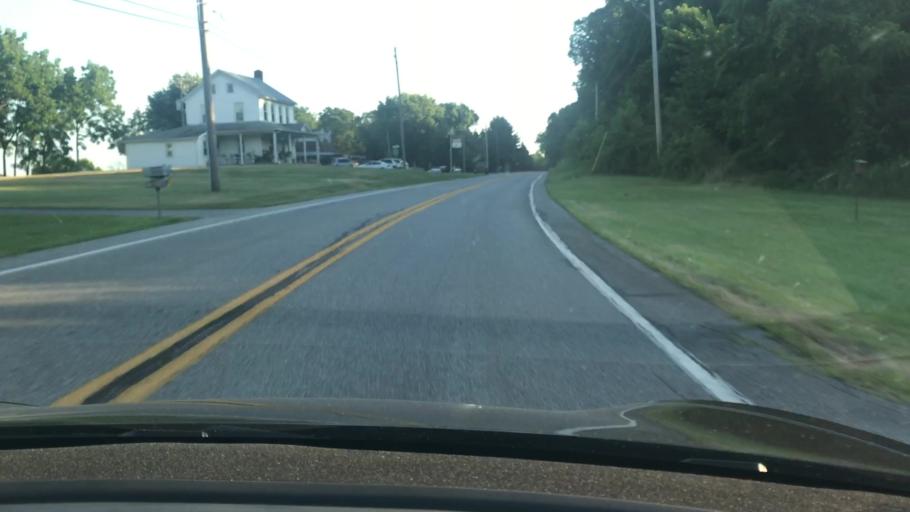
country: US
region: Pennsylvania
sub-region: York County
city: Dover
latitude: 40.0770
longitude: -76.8752
